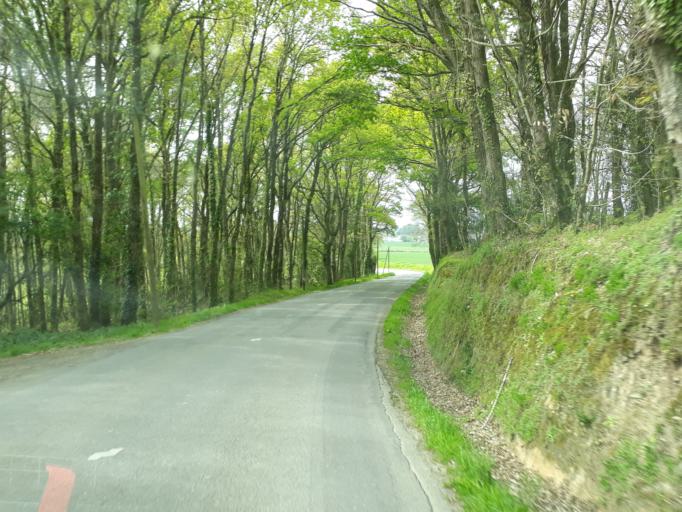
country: FR
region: Brittany
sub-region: Departement du Morbihan
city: Theix
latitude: 47.6472
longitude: -2.6343
